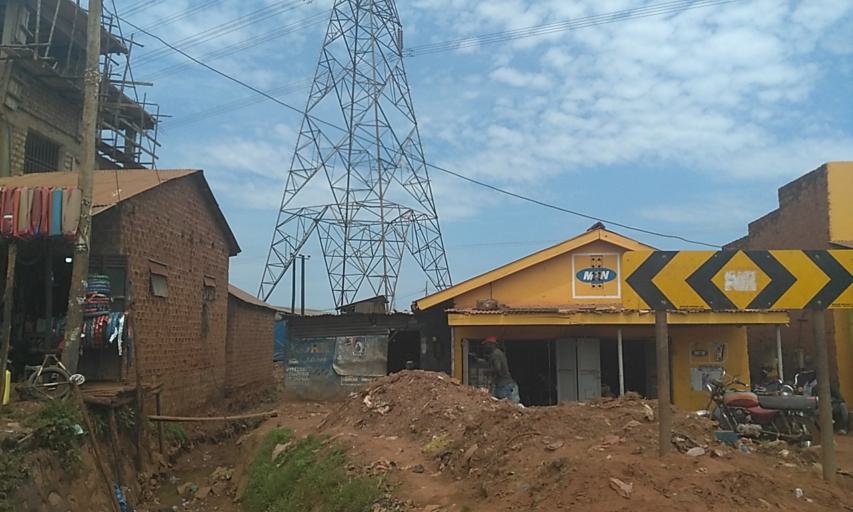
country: UG
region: Central Region
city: Kampala Central Division
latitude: 0.2973
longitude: 32.5266
